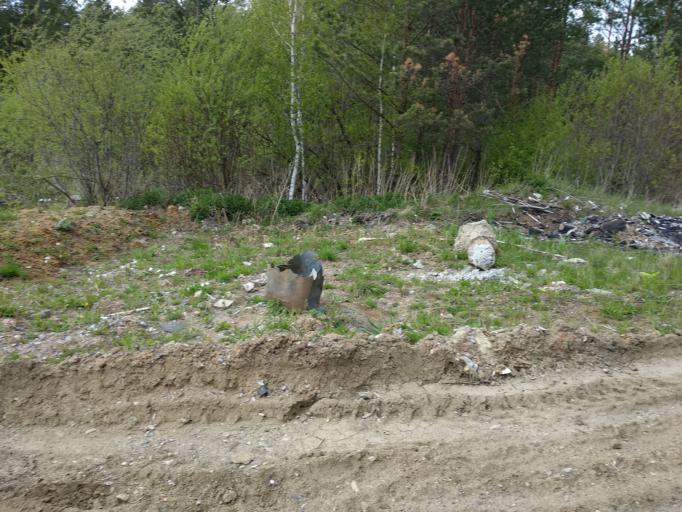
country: RU
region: Sverdlovsk
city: Beryozovsky
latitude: 56.9348
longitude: 60.7226
